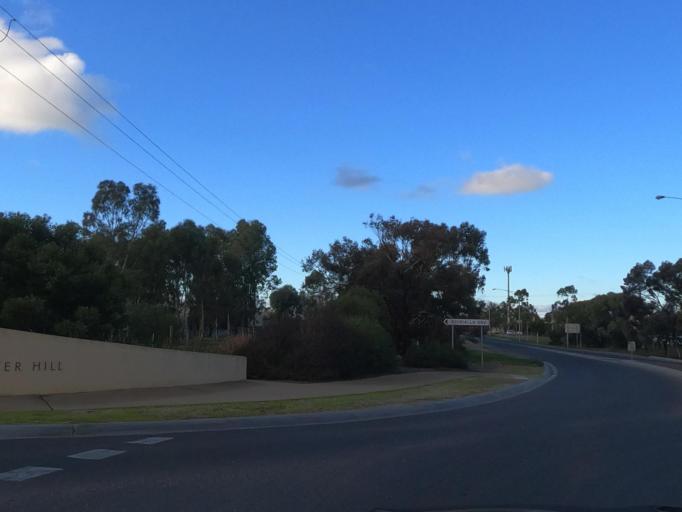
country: AU
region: Victoria
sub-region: Swan Hill
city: Swan Hill
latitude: -35.3429
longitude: 143.5315
